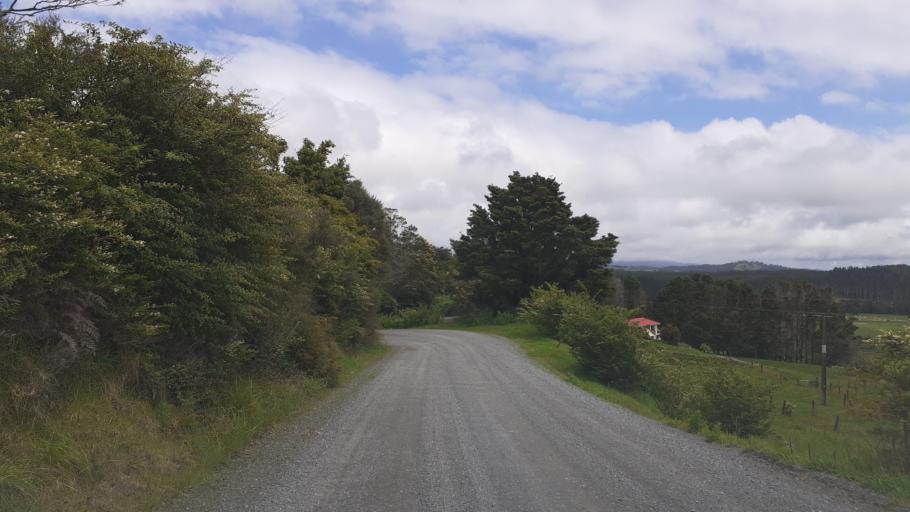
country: NZ
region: Northland
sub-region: Far North District
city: Kawakawa
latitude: -35.5152
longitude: 174.0836
